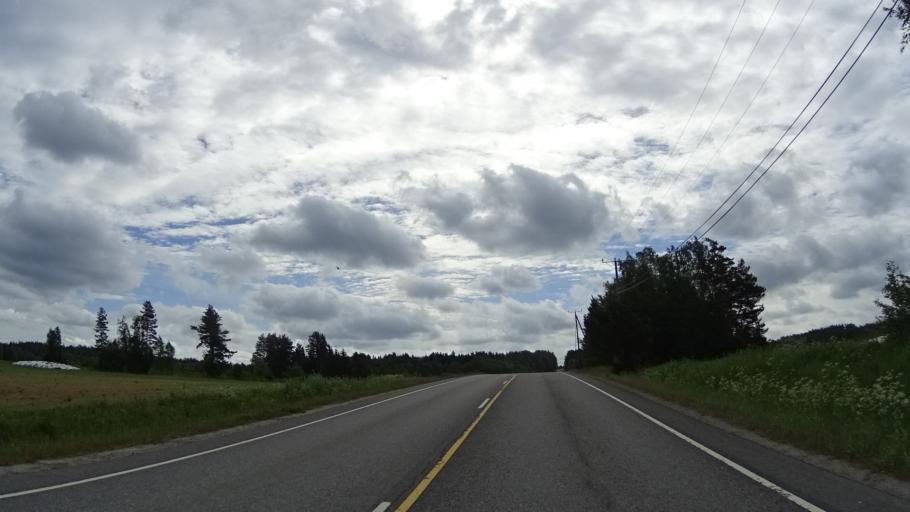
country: FI
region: Uusimaa
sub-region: Helsinki
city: Vihti
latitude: 60.2977
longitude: 24.3817
